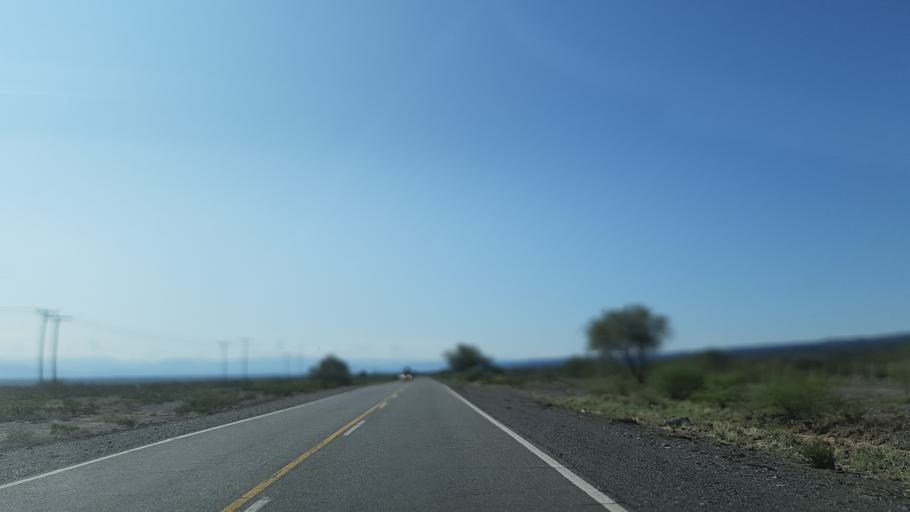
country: AR
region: San Juan
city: Caucete
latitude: -31.7503
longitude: -68.0938
